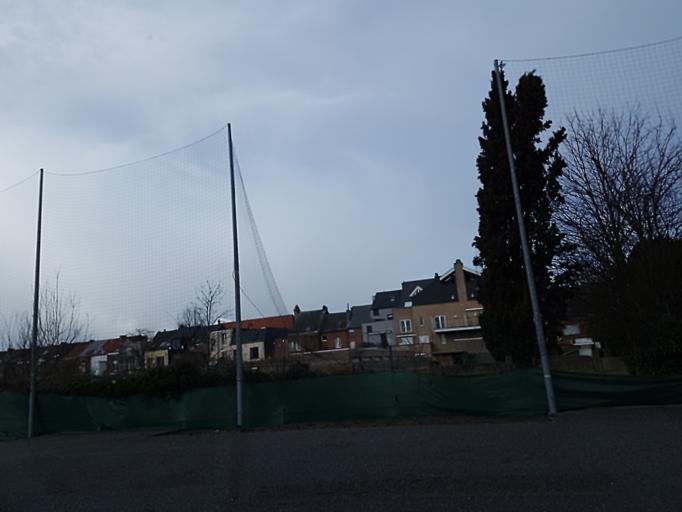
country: BE
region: Flanders
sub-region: Provincie Antwerpen
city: Mechelen
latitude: 51.0377
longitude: 4.4849
